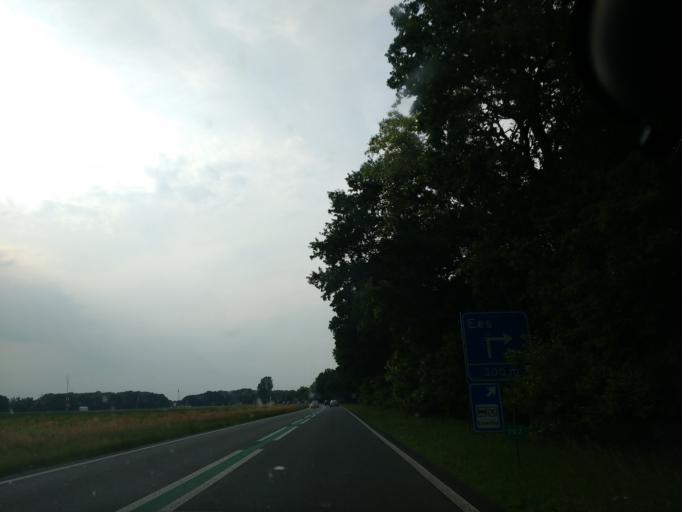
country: NL
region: Drenthe
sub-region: Gemeente Borger-Odoorn
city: Borger
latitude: 52.8970
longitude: 6.8156
